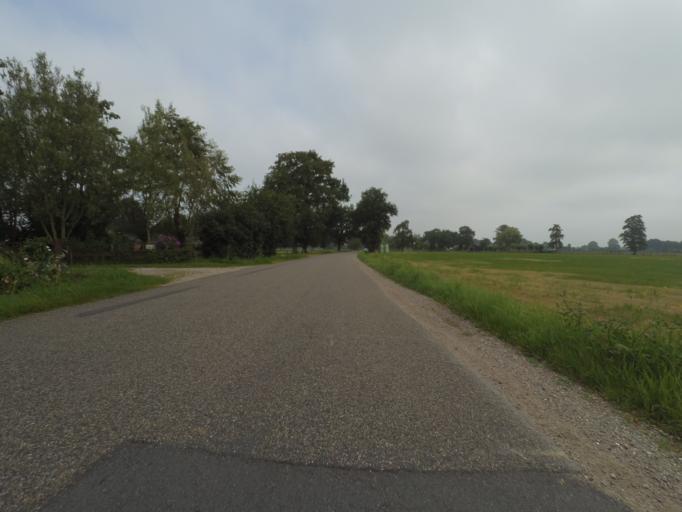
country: NL
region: Gelderland
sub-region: Gemeente Ede
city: Lunteren
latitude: 52.1122
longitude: 5.6342
